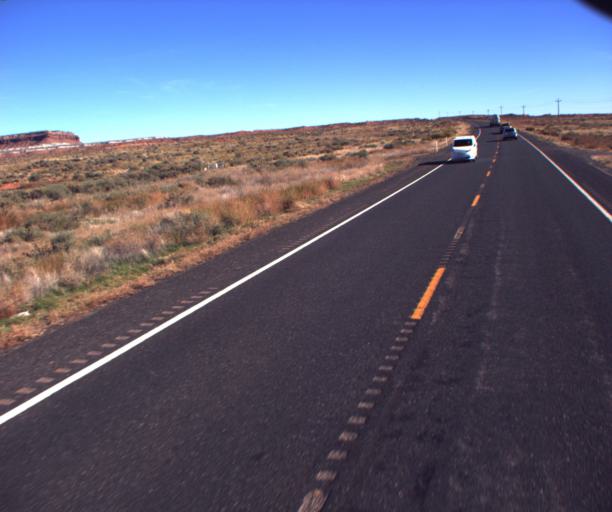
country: US
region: Arizona
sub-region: Coconino County
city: Fredonia
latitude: 36.8982
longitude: -112.6043
